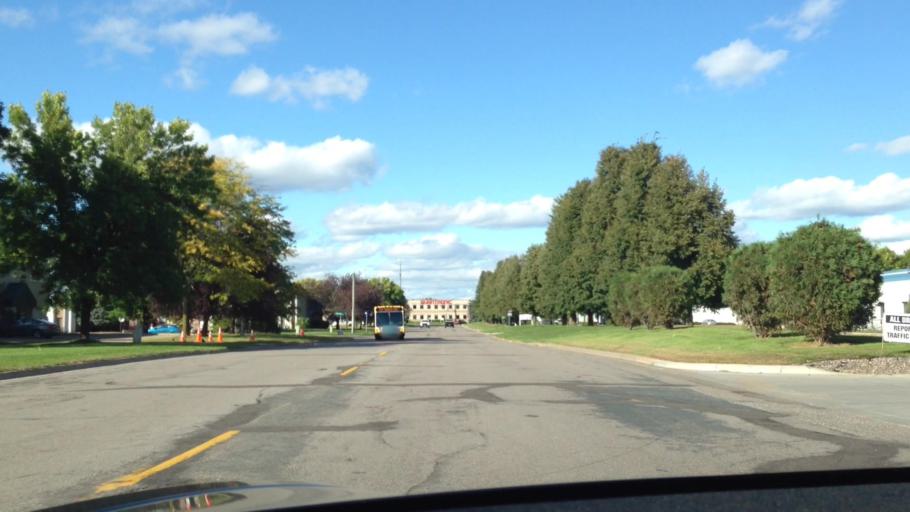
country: US
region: Minnesota
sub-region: Hennepin County
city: Osseo
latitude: 45.1133
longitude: -93.3869
